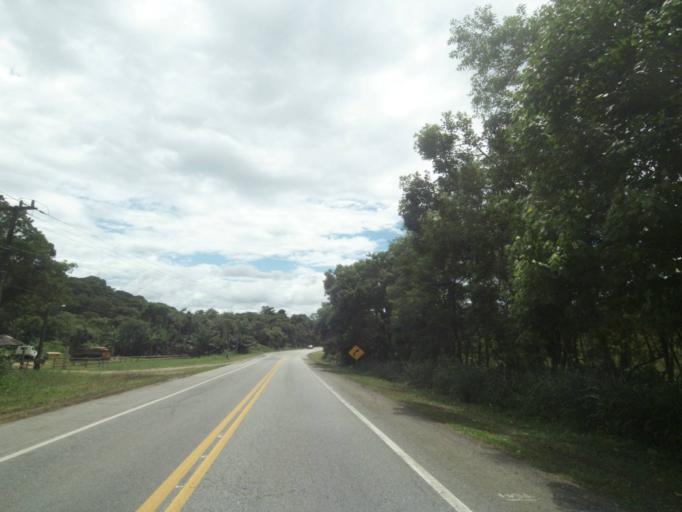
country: BR
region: Parana
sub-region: Antonina
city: Antonina
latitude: -25.4479
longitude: -48.7722
